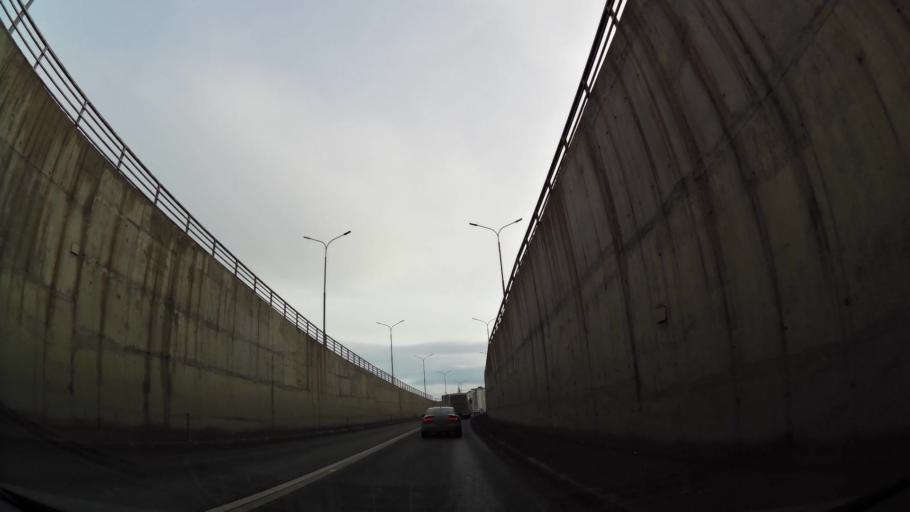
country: XK
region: Pristina
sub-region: Komuna e Prishtines
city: Pristina
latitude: 42.6456
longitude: 21.1560
